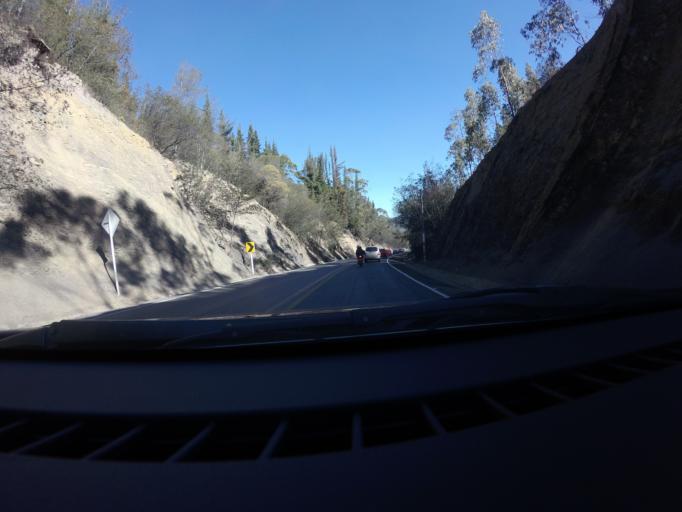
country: CO
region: Cundinamarca
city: Sutatausa
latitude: 5.2389
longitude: -73.8562
